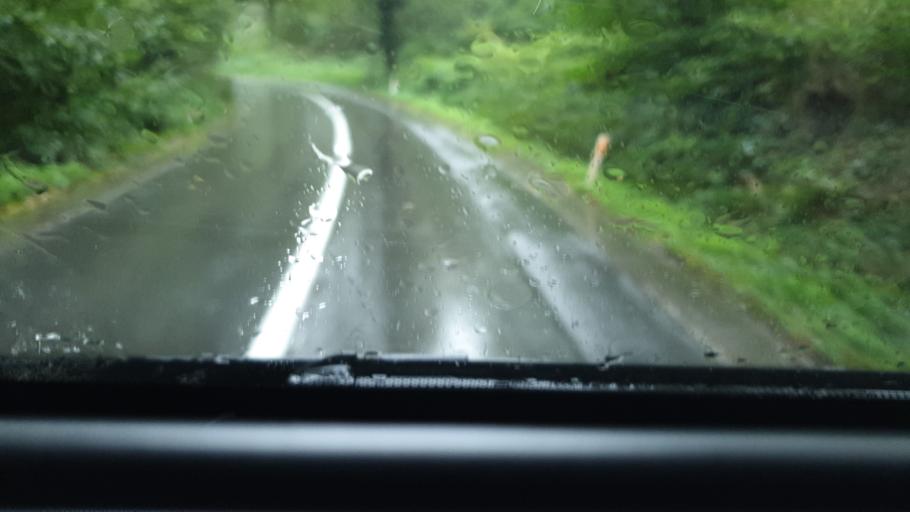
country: BE
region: Wallonia
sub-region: Province du Hainaut
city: Charleroi
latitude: 50.3665
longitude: 4.4772
